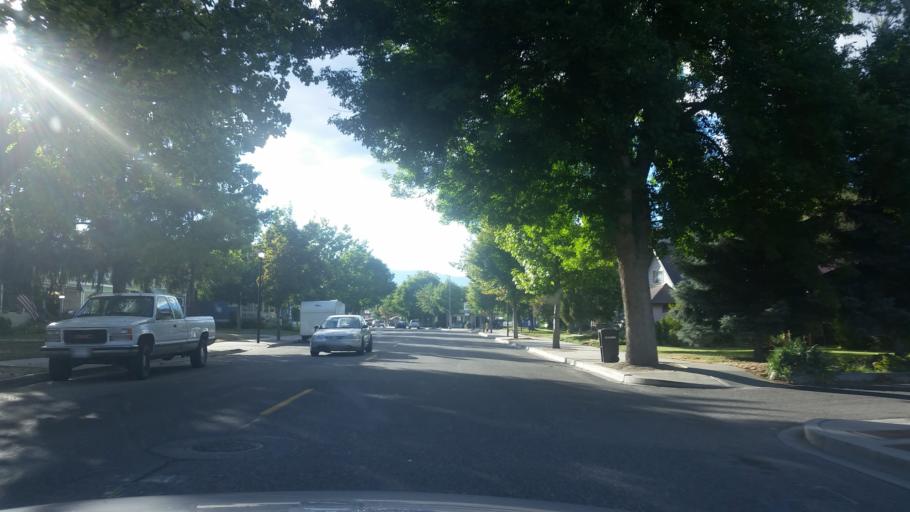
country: US
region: Washington
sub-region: Chelan County
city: Cashmere
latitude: 47.5212
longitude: -120.4642
